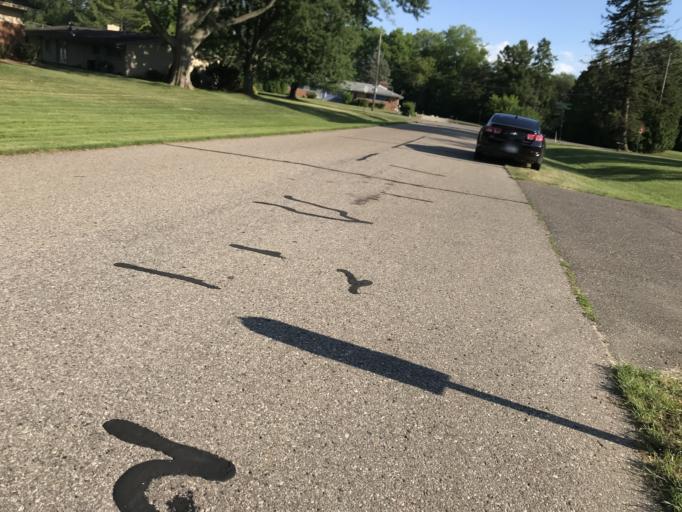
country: US
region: Michigan
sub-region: Oakland County
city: Farmington
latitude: 42.4666
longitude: -83.3248
